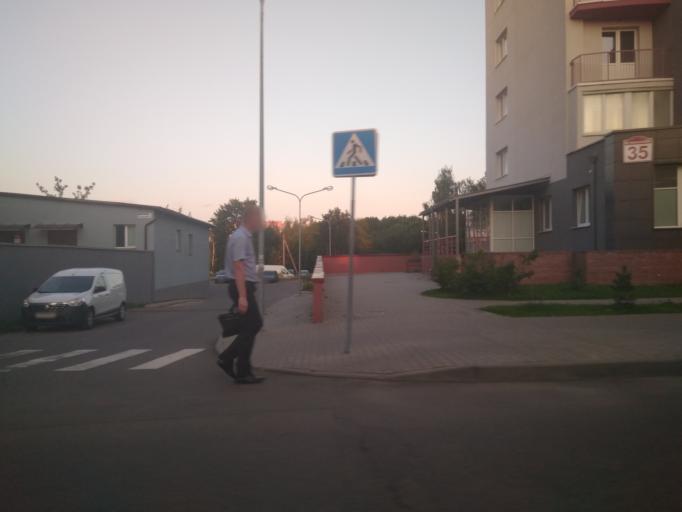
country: BY
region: Minsk
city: Novoye Medvezhino
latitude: 53.9291
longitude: 27.4783
